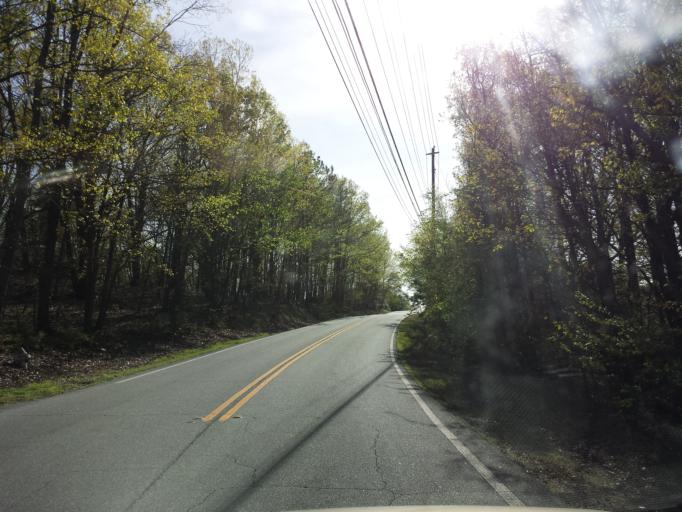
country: US
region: Georgia
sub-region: Cobb County
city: Marietta
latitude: 33.9730
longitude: -84.5004
